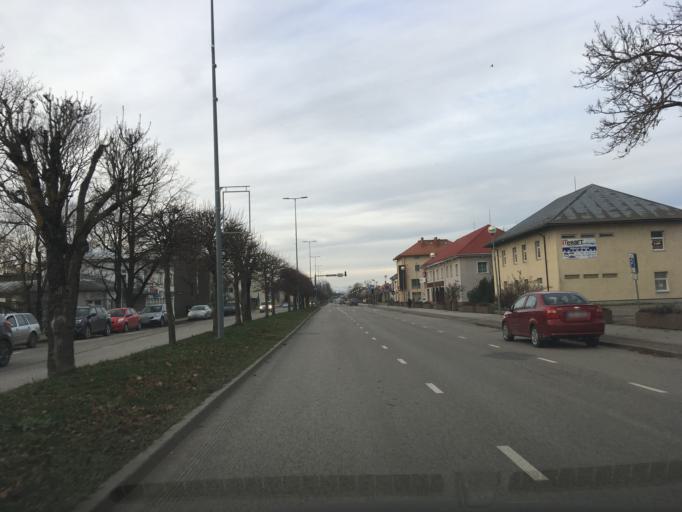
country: EE
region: Ida-Virumaa
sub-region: Johvi vald
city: Johvi
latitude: 59.3596
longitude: 27.4074
